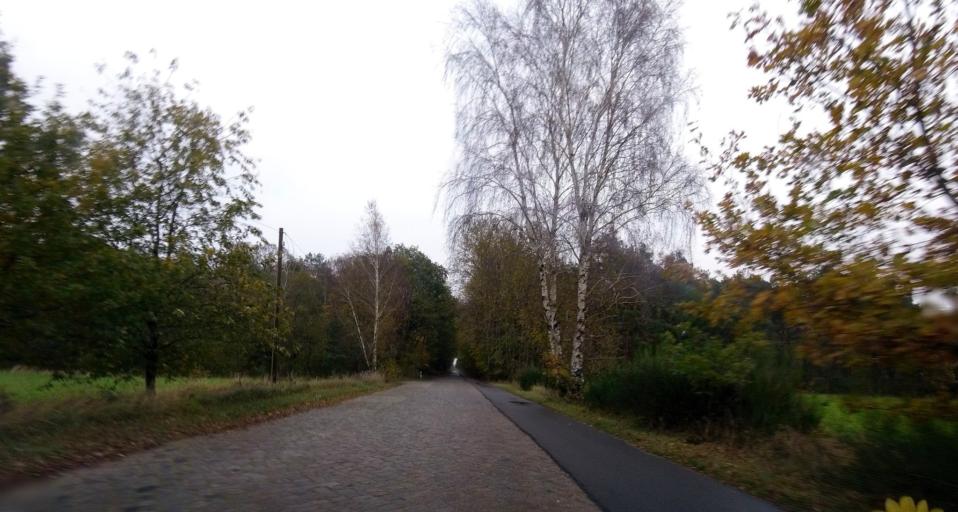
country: DE
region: Brandenburg
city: Niedergorsdorf
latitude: 51.9998
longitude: 12.9704
